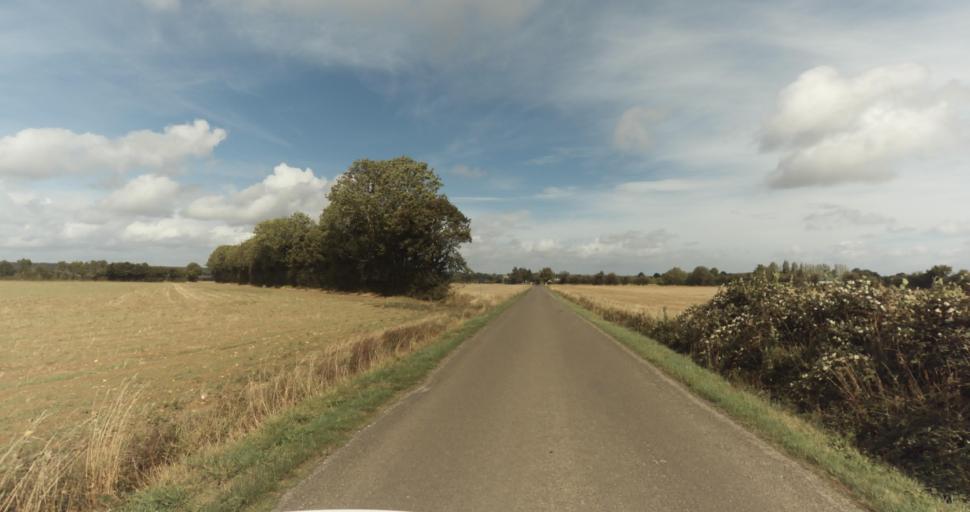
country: FR
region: Lower Normandy
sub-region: Departement de l'Orne
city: Gace
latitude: 48.8196
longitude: 0.3839
